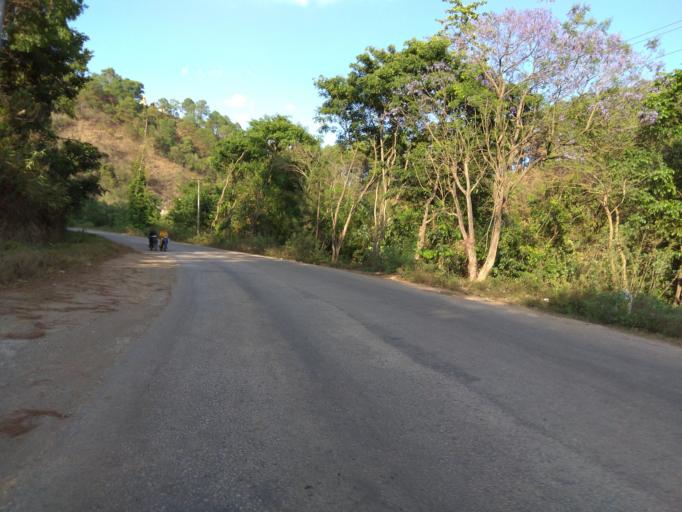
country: MM
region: Shan
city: Taunggyi
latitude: 20.6323
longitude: 96.5813
